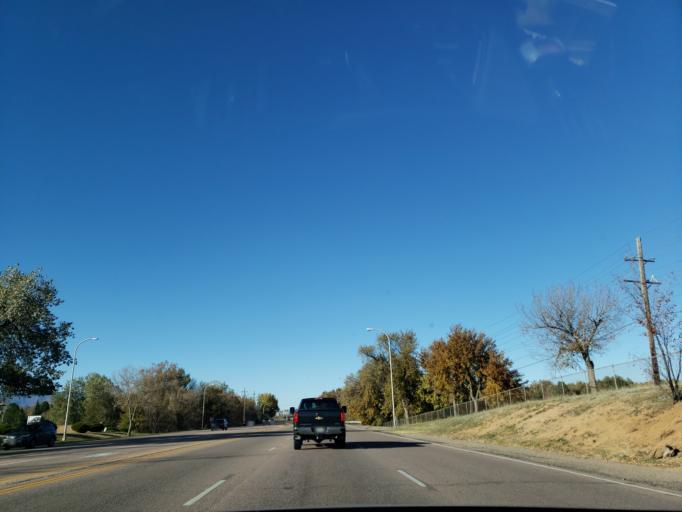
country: US
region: Colorado
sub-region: El Paso County
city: Colorado Springs
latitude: 38.7901
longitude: -104.8220
